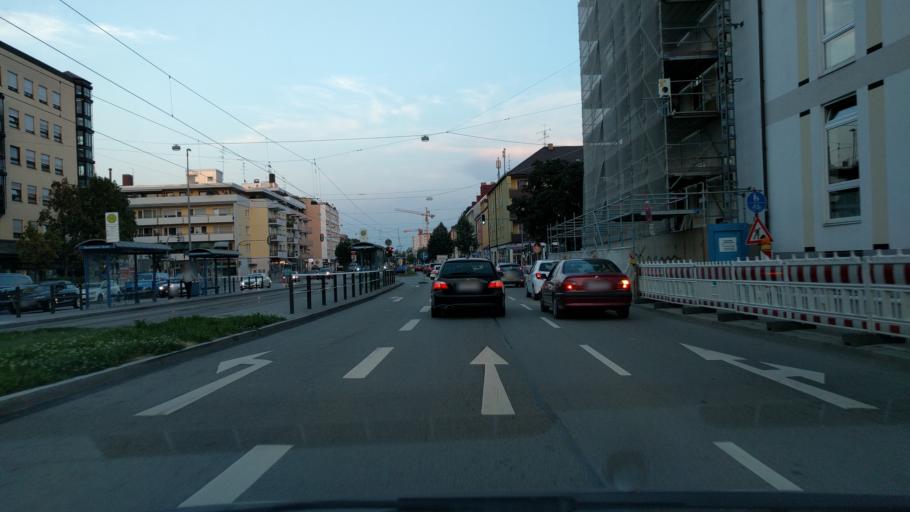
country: DE
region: Bavaria
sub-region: Upper Bavaria
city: Bogenhausen
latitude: 48.1285
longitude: 11.6294
